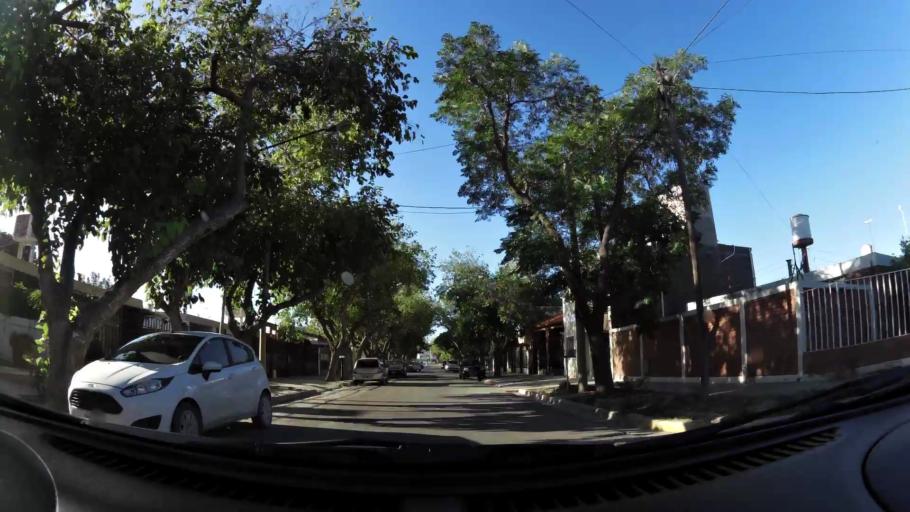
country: AR
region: San Juan
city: San Juan
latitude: -31.5503
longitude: -68.5195
